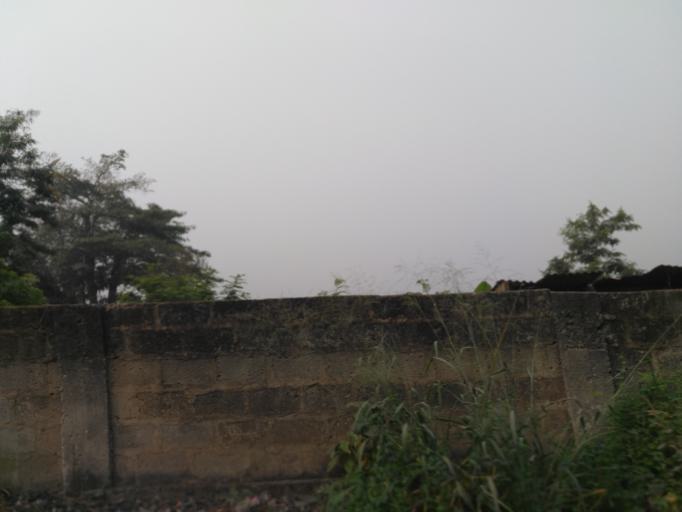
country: GH
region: Ashanti
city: Kumasi
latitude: 6.6520
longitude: -1.6197
